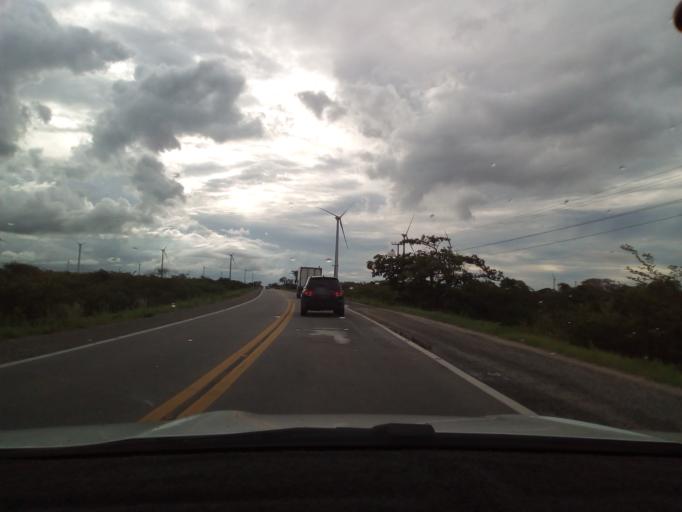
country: BR
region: Ceara
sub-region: Aracati
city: Aracati
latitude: -4.6000
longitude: -37.6690
